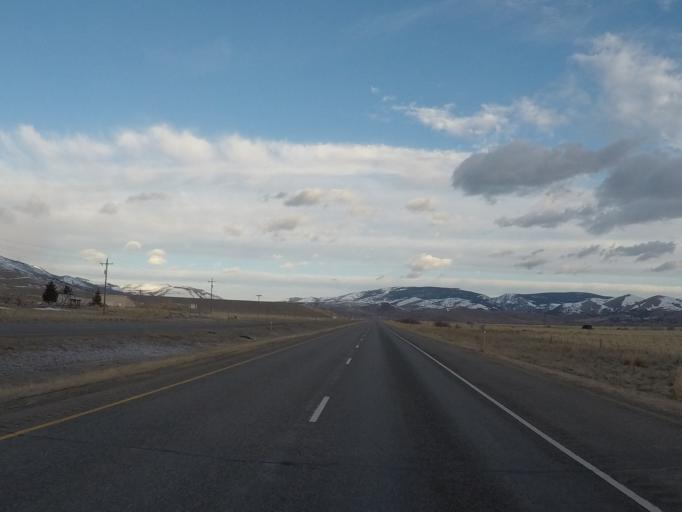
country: US
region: Montana
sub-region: Deer Lodge County
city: Anaconda
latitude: 46.1126
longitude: -112.8603
